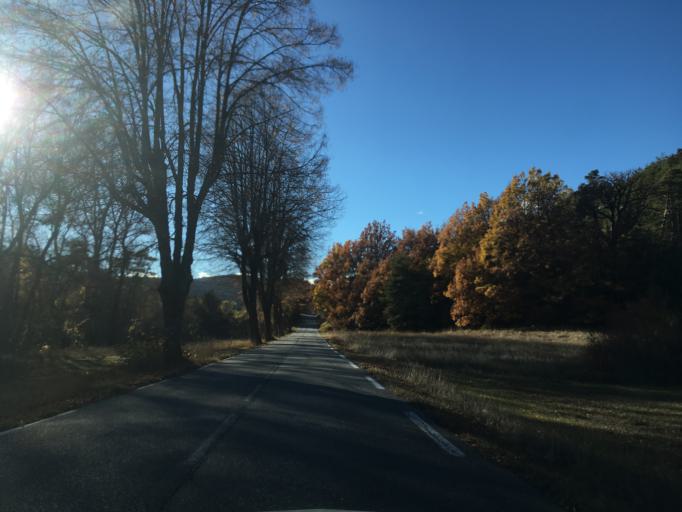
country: FR
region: Provence-Alpes-Cote d'Azur
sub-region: Departement des Alpes-de-Haute-Provence
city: Castellane
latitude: 43.7421
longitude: 6.4963
